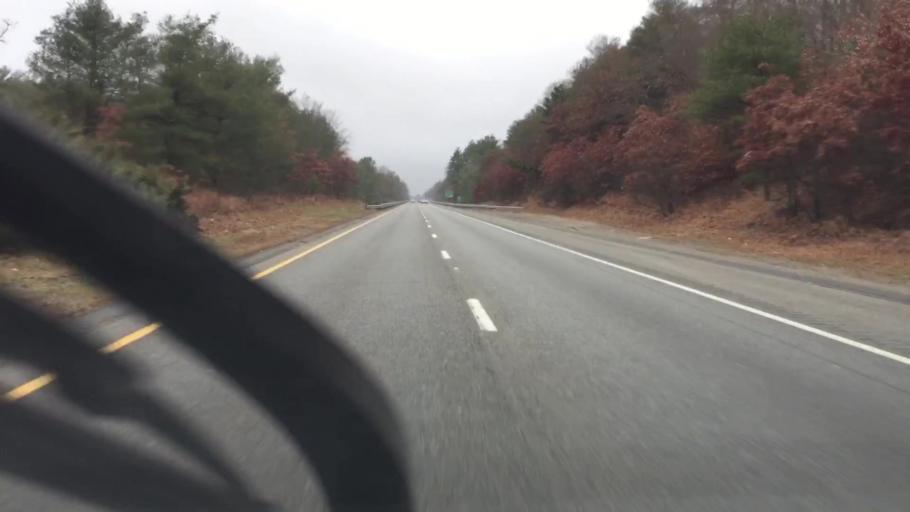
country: US
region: Massachusetts
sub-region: Bristol County
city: Raynham Center
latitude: 41.9257
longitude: -70.9988
